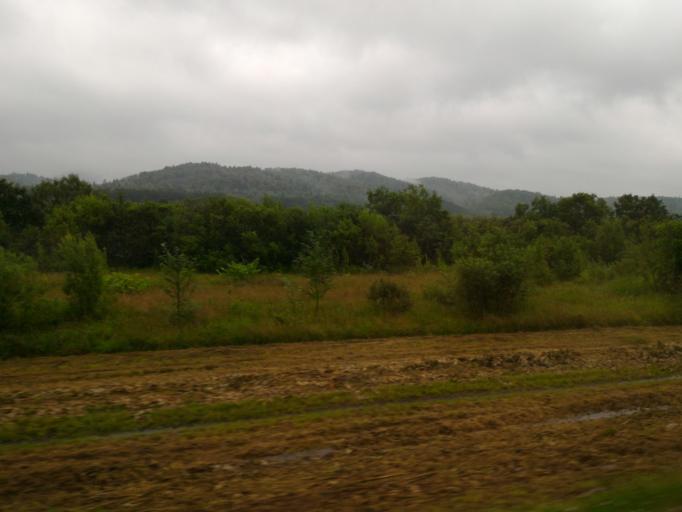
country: JP
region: Hokkaido
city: Nayoro
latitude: 44.7586
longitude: 142.0500
